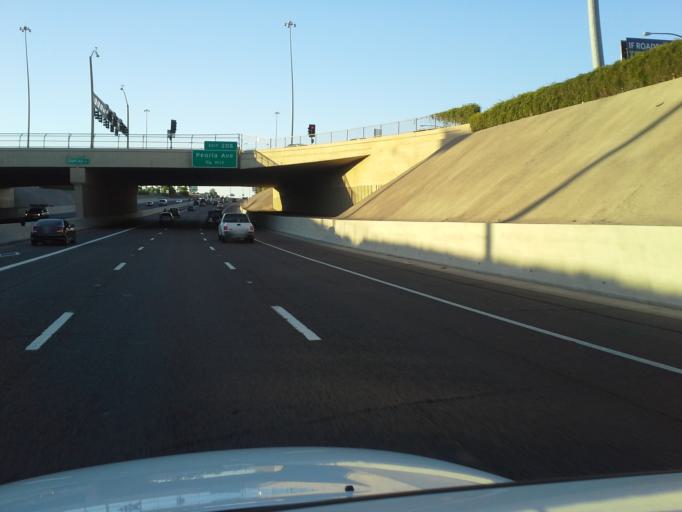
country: US
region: Arizona
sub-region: Maricopa County
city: Glendale
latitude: 33.5667
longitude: -112.1171
